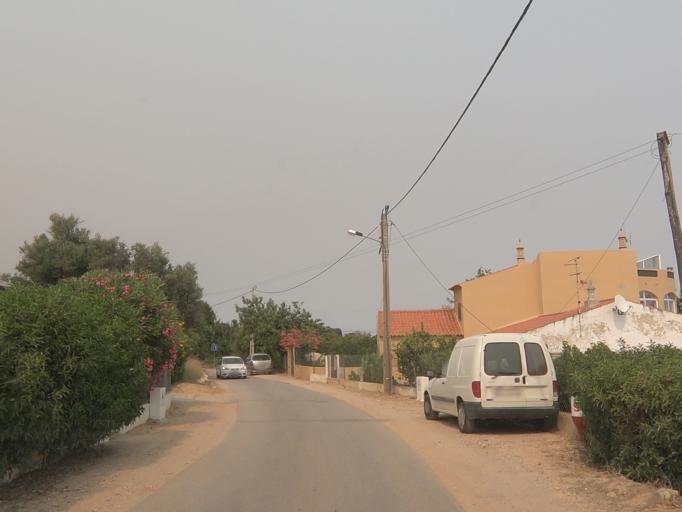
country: PT
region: Faro
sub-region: Lagoa
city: Carvoeiro
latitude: 37.0961
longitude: -8.4086
